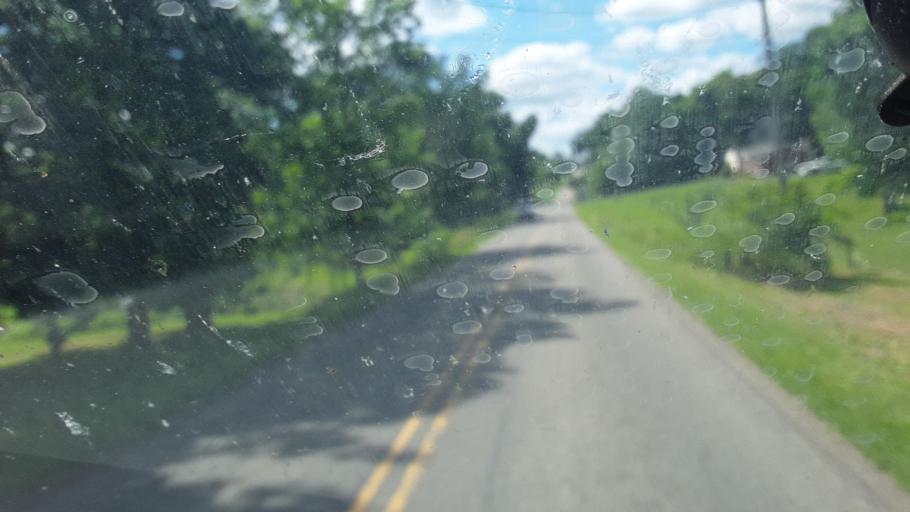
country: US
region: Pennsylvania
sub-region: Lawrence County
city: New Wilmington
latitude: 41.0777
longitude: -80.2633
